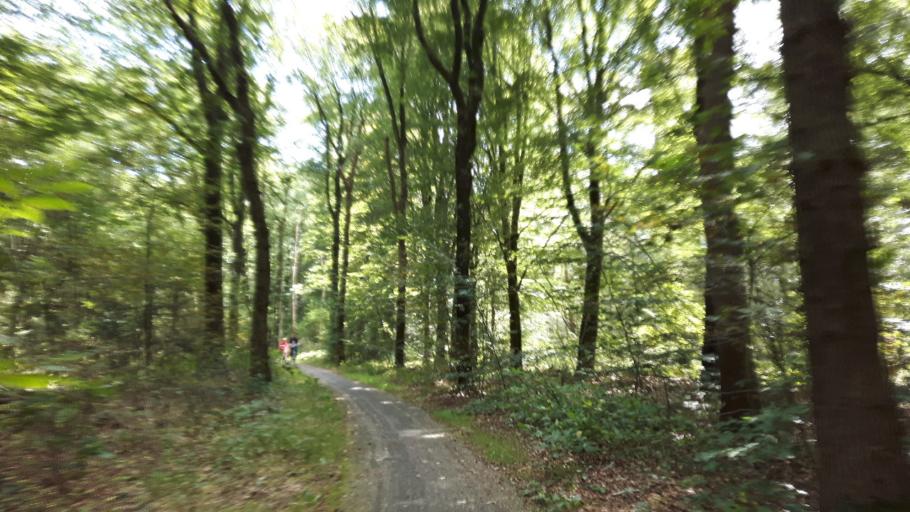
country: NL
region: Friesland
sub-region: Gemeente Smallingerland
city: Drachtstercompagnie
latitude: 53.0700
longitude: 6.2045
